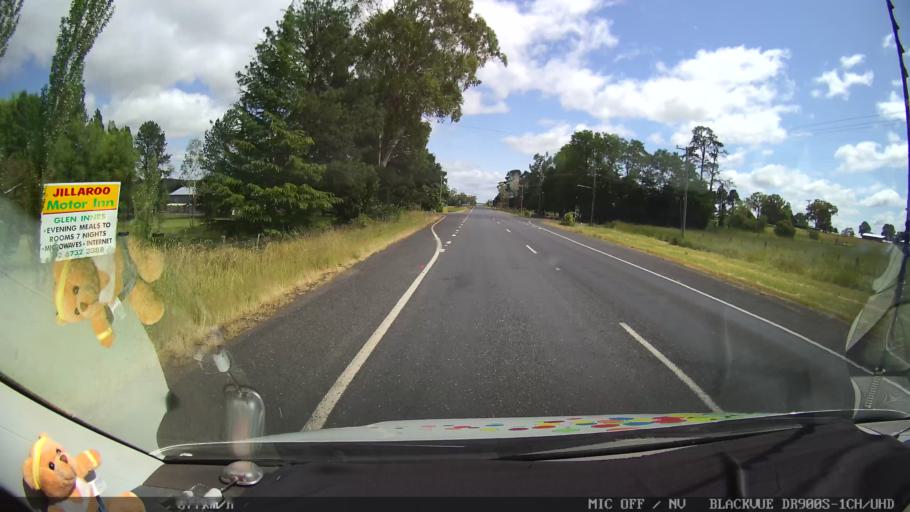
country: AU
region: New South Wales
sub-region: Glen Innes Severn
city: Glen Innes
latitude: -29.7695
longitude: 151.7321
